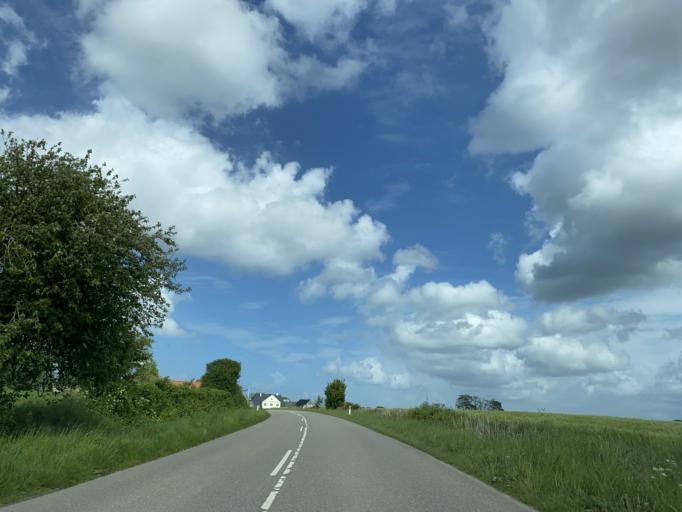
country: DK
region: South Denmark
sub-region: Sonderborg Kommune
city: Dybbol
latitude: 54.9726
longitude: 9.7129
